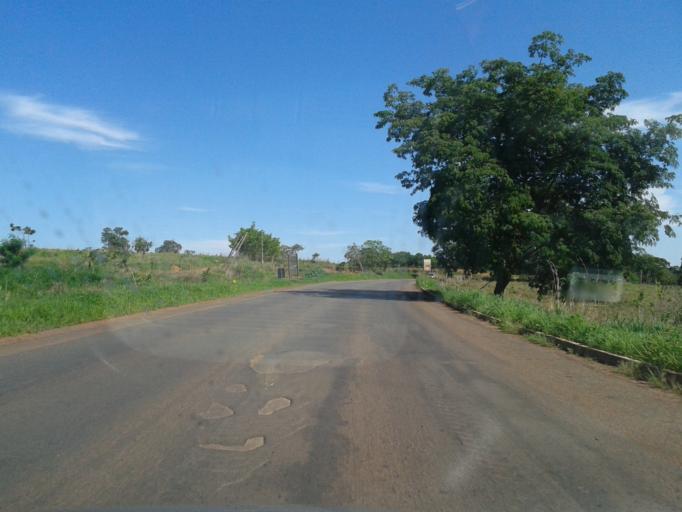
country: BR
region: Goias
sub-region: Piracanjuba
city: Piracanjuba
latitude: -17.2295
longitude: -48.7129
